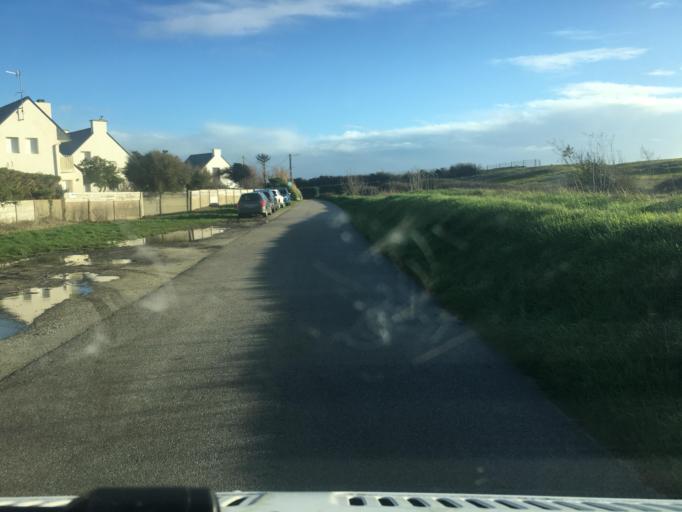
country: FR
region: Brittany
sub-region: Departement du Morbihan
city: Sarzeau
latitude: 47.4984
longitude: -2.6873
